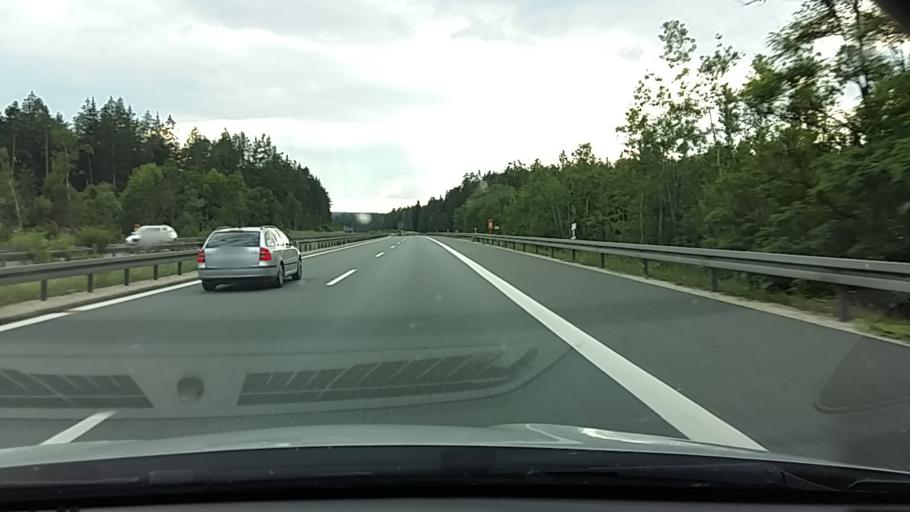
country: DE
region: Bavaria
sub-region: Upper Palatinate
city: Kummersbruck
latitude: 49.3965
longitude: 11.8608
